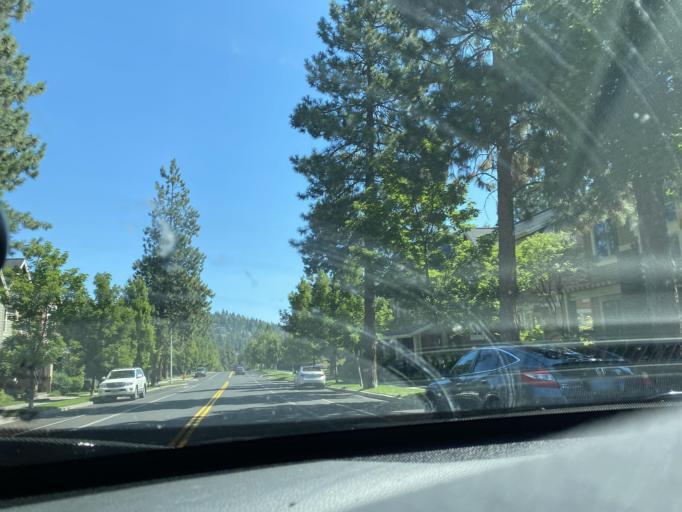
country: US
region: Oregon
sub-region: Deschutes County
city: Bend
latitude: 44.0600
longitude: -121.3494
